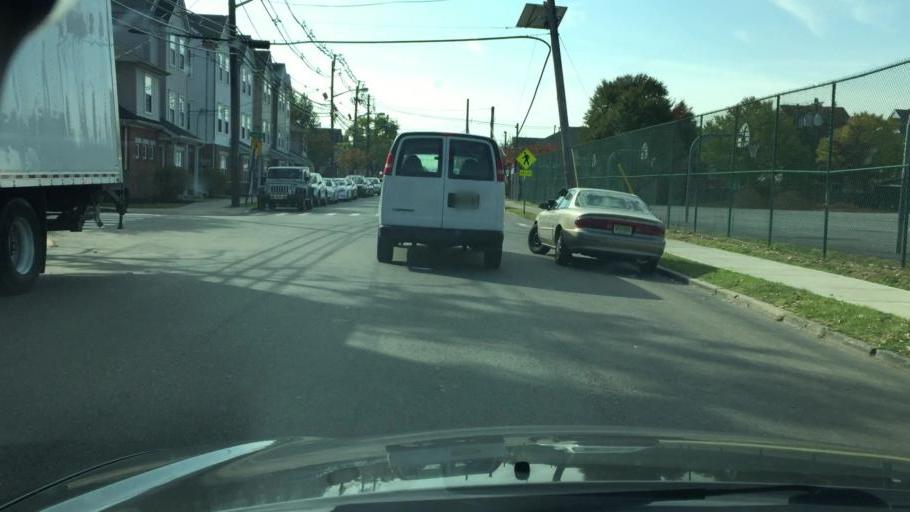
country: US
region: New Jersey
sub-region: Union County
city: Elizabeth
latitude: 40.6563
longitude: -74.1834
